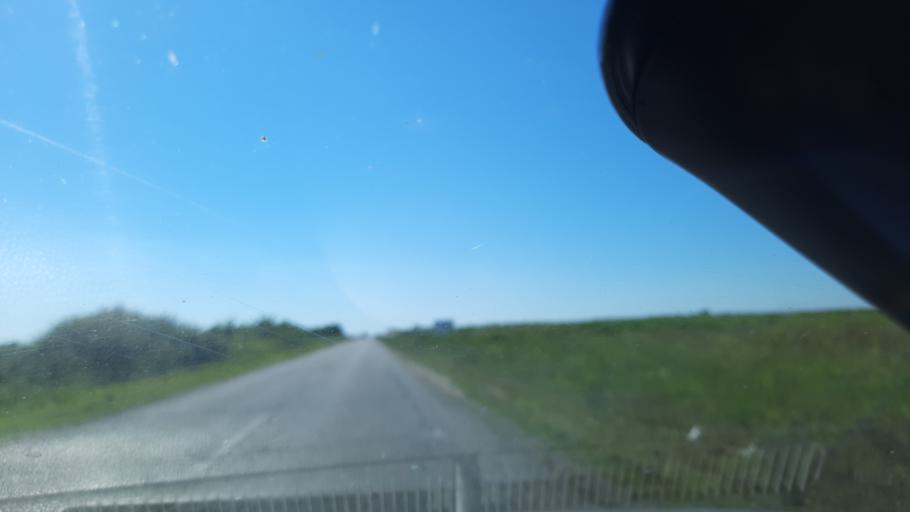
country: RS
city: Simanovci
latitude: 44.8779
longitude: 20.0664
